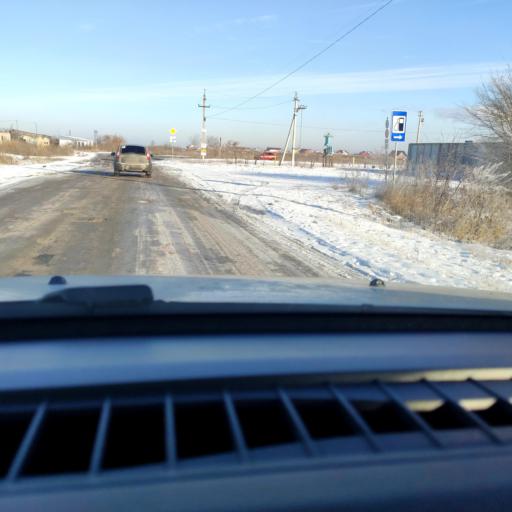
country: RU
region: Samara
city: Podstepki
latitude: 53.5222
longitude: 49.1458
